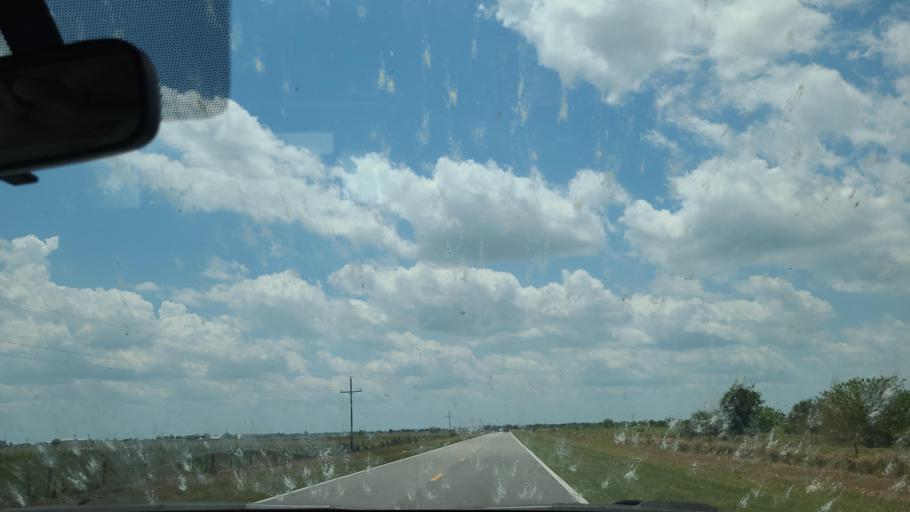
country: US
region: Florida
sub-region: Glades County
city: Buckhead Ridge
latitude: 27.2483
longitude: -81.0539
